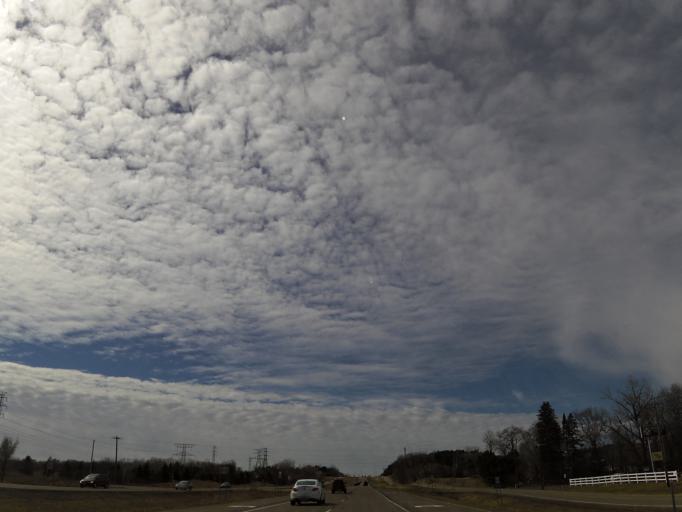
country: US
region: Minnesota
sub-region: Washington County
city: Lake Elmo
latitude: 45.0358
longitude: -92.9024
